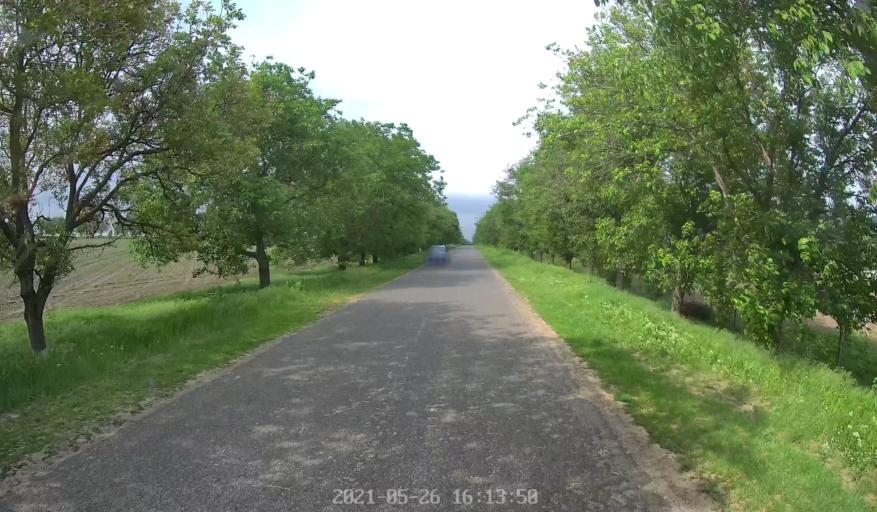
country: MD
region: Hincesti
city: Dancu
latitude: 46.7046
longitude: 28.3393
